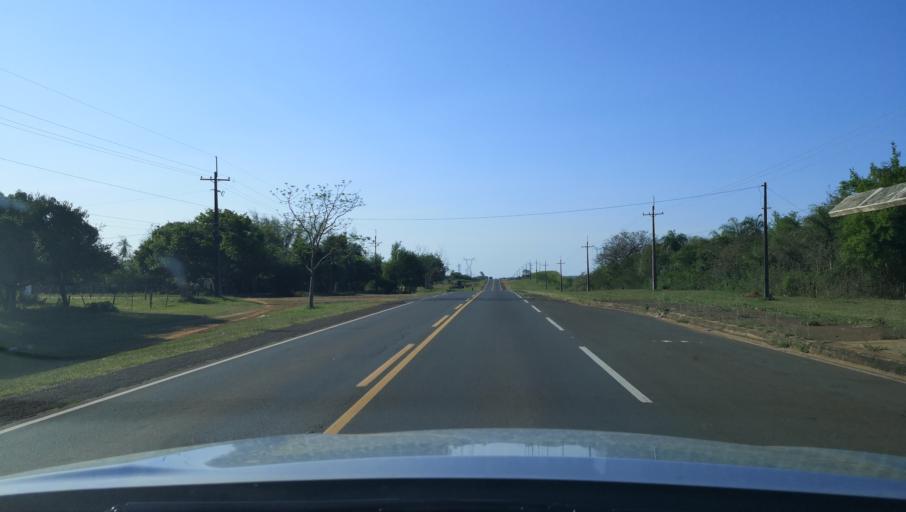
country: PY
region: Misiones
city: Santa Maria
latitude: -26.7997
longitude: -57.0219
